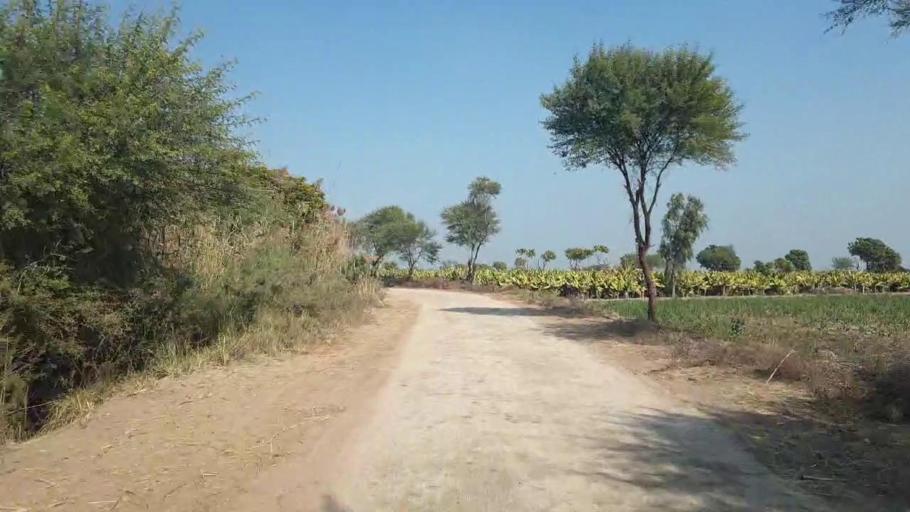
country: PK
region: Sindh
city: Shahdadpur
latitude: 25.9754
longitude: 68.5289
